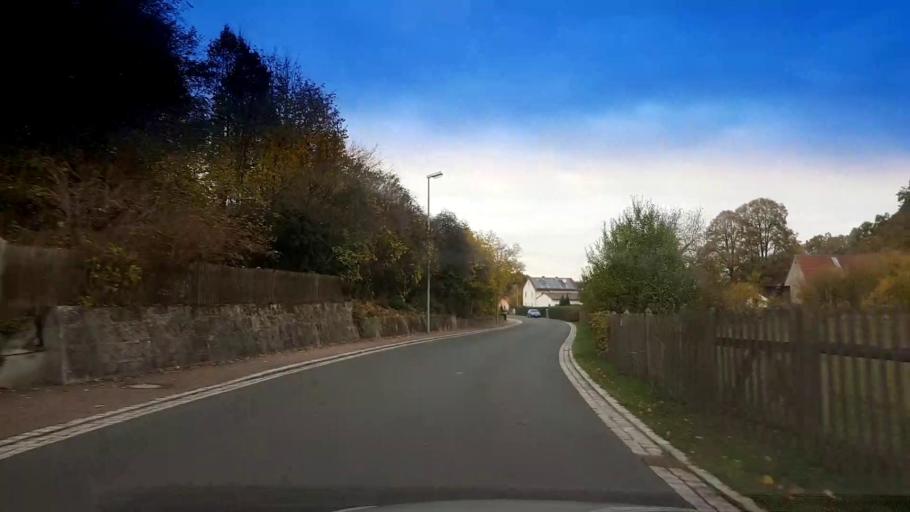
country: DE
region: Bavaria
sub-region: Upper Franconia
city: Priesendorf
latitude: 49.9306
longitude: 10.6935
